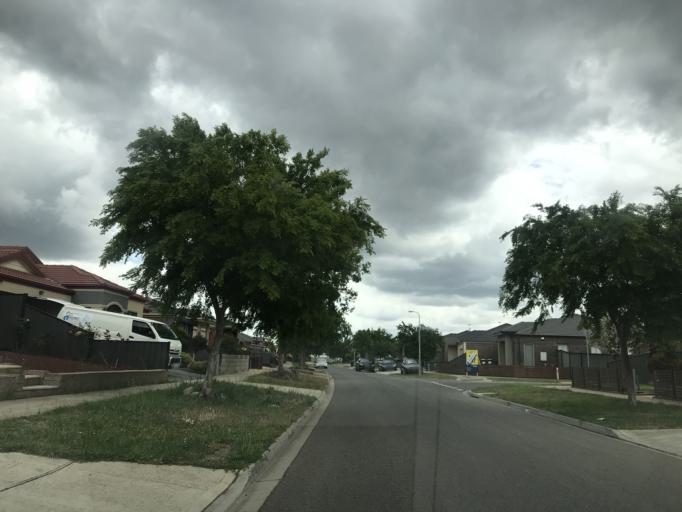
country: AU
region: Victoria
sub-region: Brimbank
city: Derrimut
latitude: -37.7868
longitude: 144.7571
